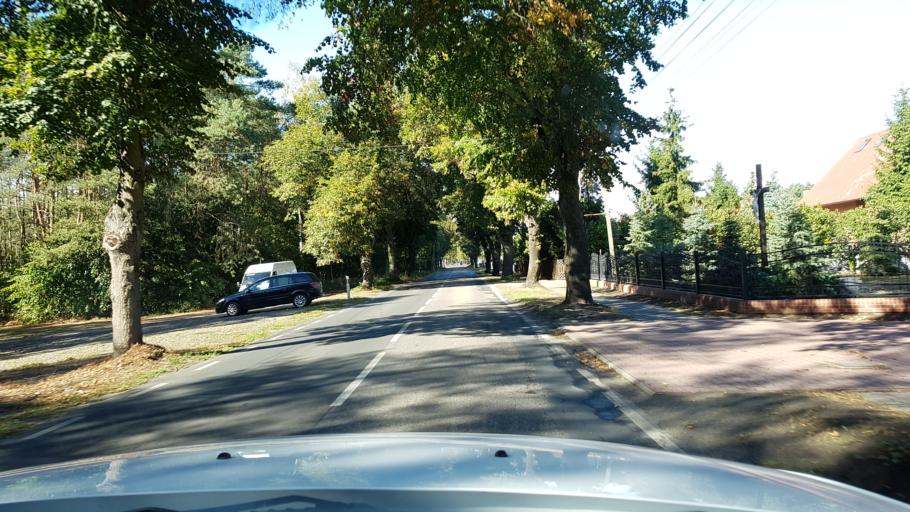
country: PL
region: West Pomeranian Voivodeship
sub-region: Powiat gryfinski
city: Gryfino
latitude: 53.2136
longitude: 14.4976
